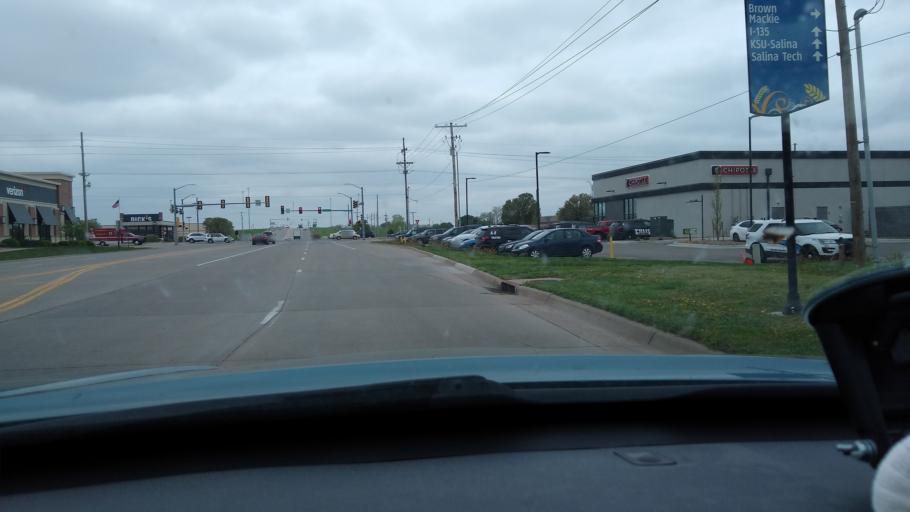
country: US
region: Kansas
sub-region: Saline County
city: Salina
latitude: 38.7982
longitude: -97.6114
